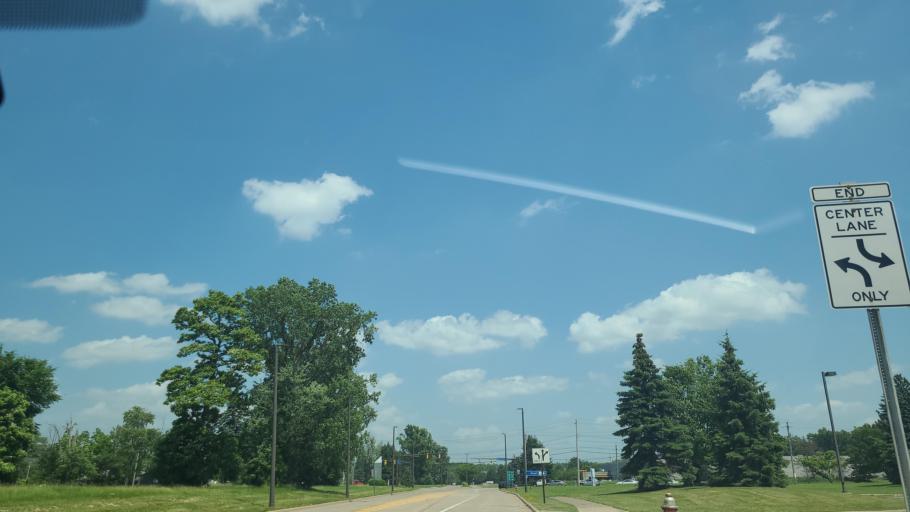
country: US
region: Ohio
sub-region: Cuyahoga County
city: Brook Park
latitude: 41.4251
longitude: -81.8302
